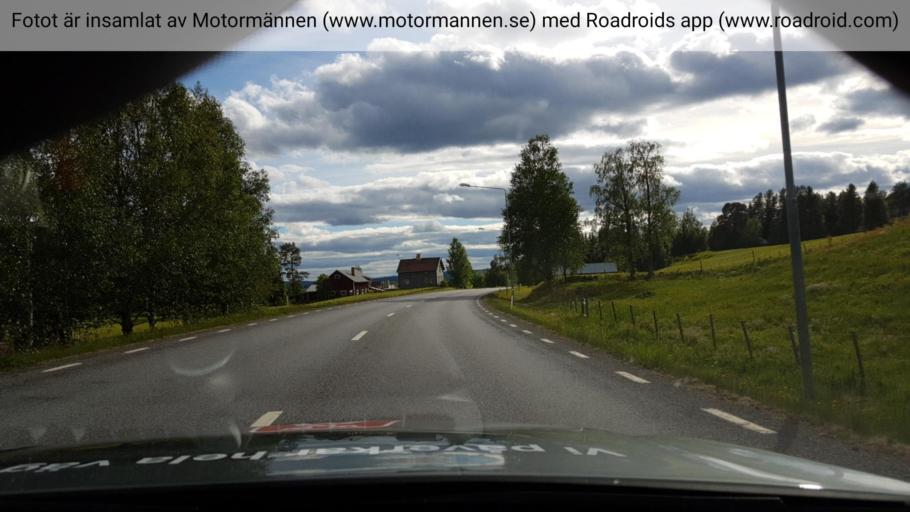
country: SE
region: Jaemtland
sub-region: OEstersunds Kommun
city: Lit
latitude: 63.3910
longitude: 14.9638
